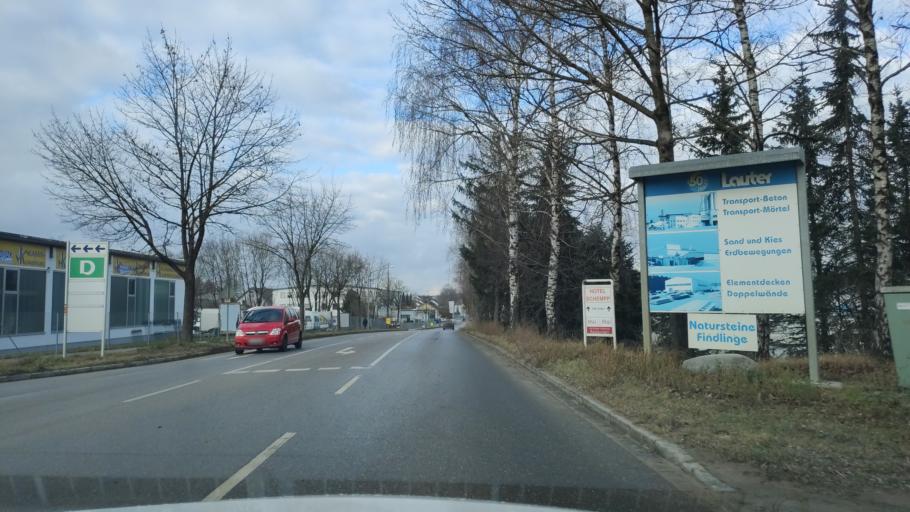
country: DE
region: Bavaria
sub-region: Swabia
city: Bobingen
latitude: 48.2732
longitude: 10.8486
